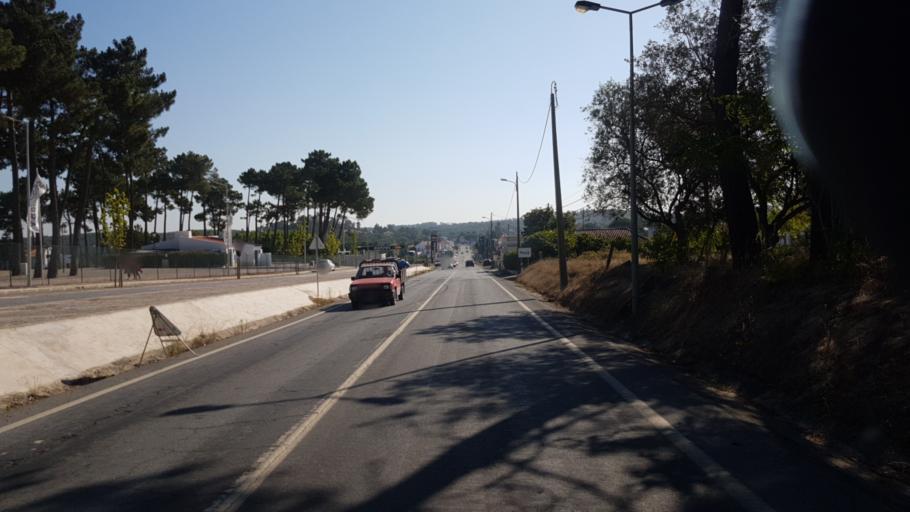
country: PT
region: Setubal
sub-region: Sesimbra
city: Sesimbra
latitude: 38.4720
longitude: -9.0851
